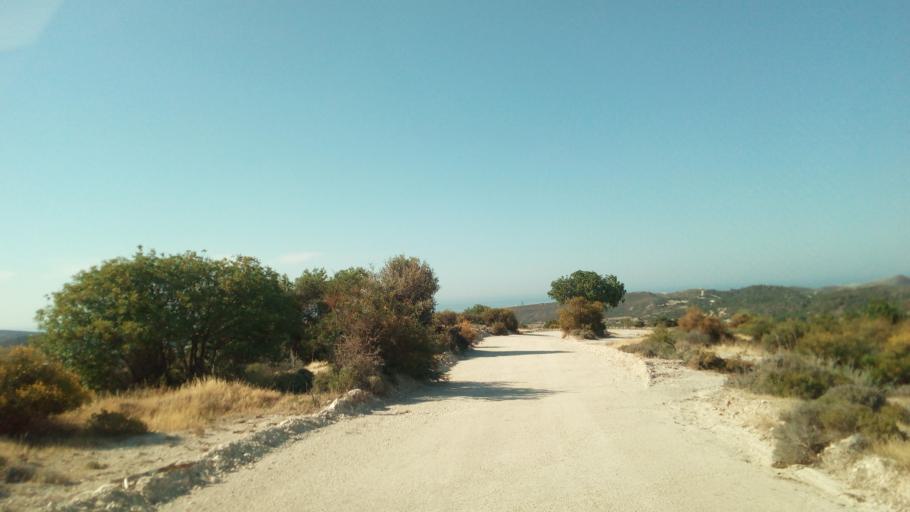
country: CY
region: Larnaka
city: Kofinou
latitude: 34.8104
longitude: 33.3147
